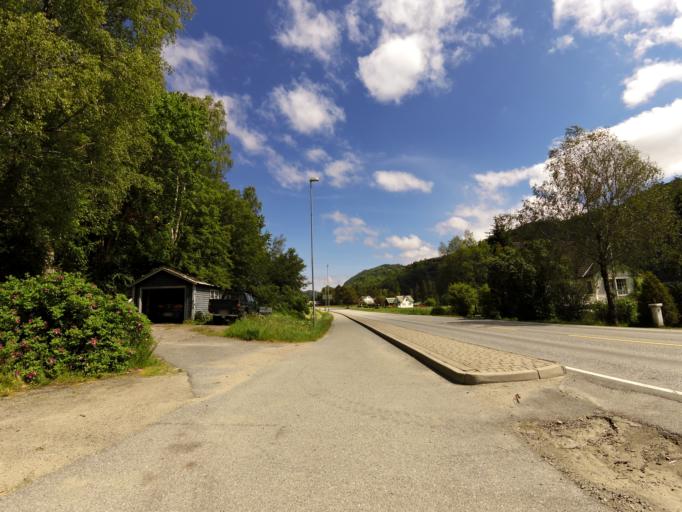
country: NO
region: Vest-Agder
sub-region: Kvinesdal
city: Liknes
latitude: 58.3053
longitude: 6.9527
